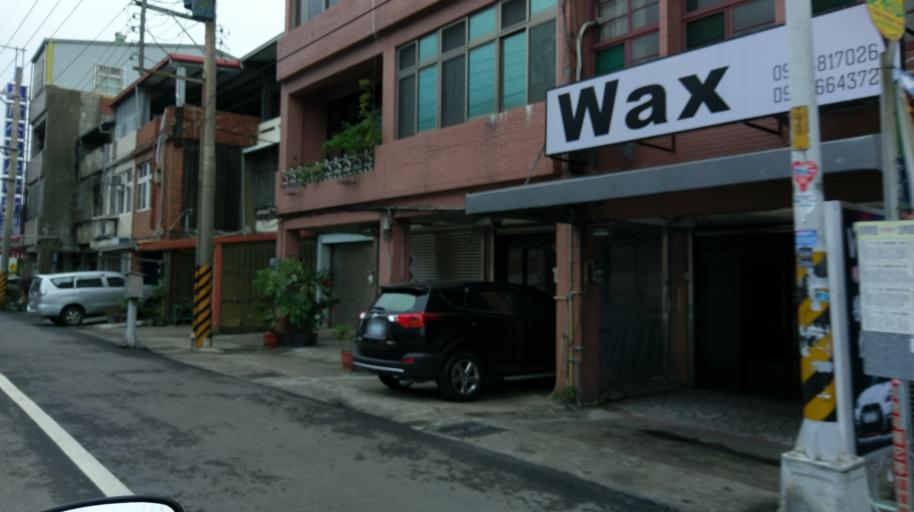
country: TW
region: Taiwan
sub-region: Miaoli
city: Miaoli
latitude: 24.6791
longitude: 120.9000
